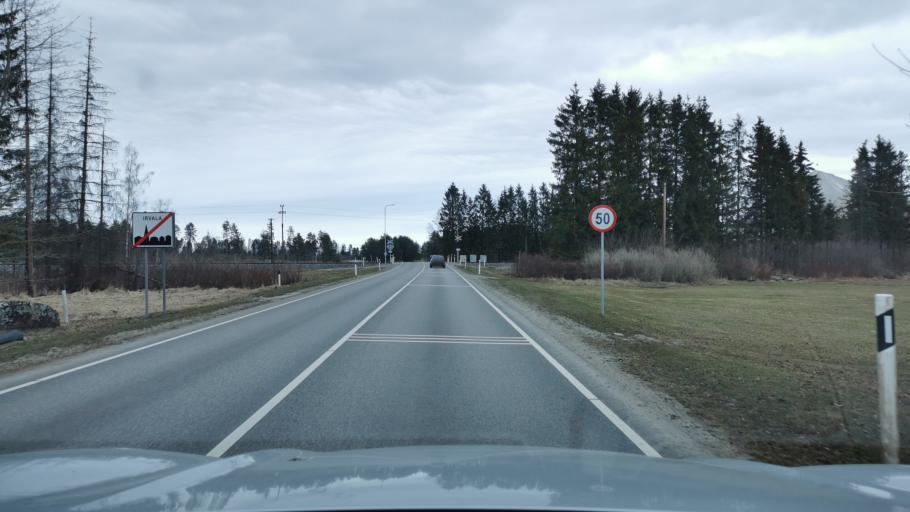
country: EE
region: Ida-Virumaa
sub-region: Puessi linn
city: Pussi
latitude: 59.3559
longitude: 27.0223
